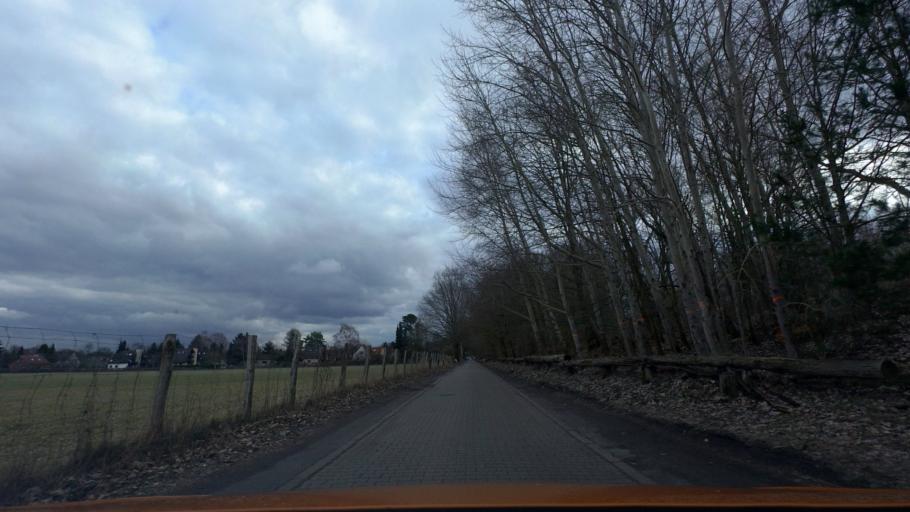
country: DE
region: Berlin
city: Konradshohe
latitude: 52.5997
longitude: 13.2328
